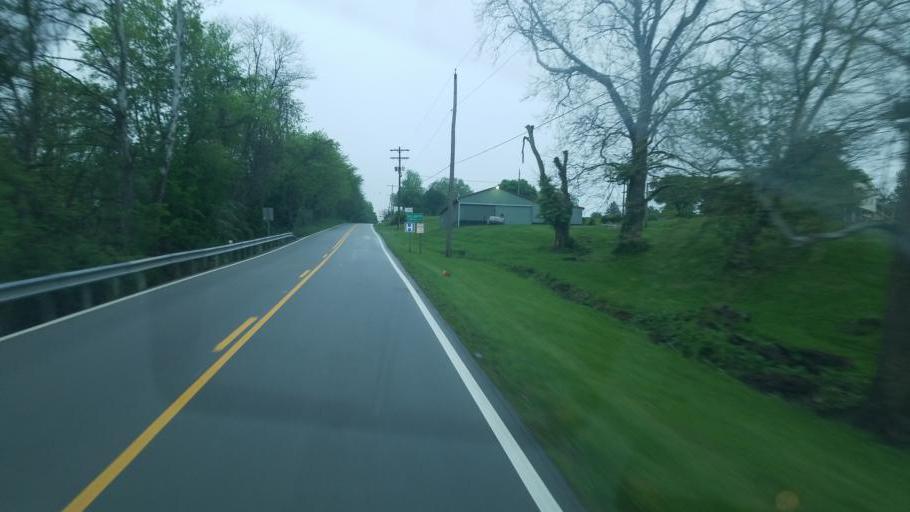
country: US
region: Ohio
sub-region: Highland County
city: Hillsboro
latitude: 39.1967
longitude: -83.6321
